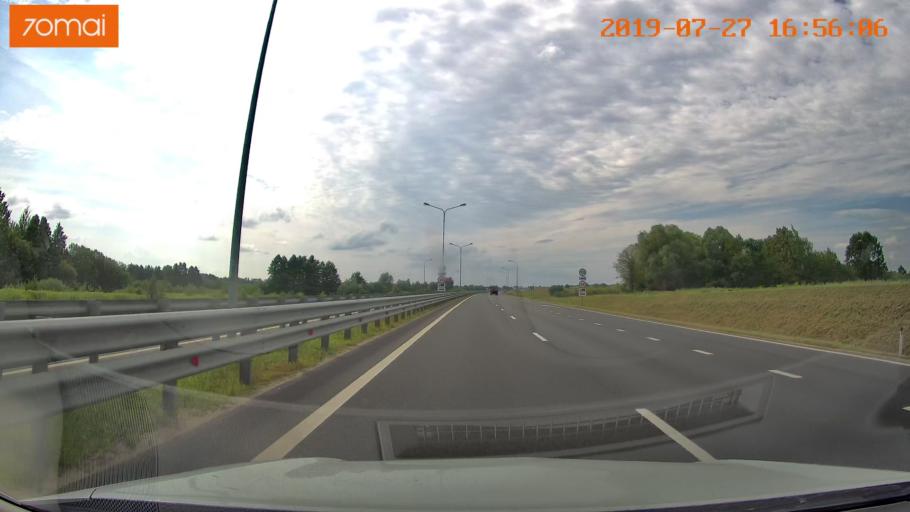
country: RU
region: Kaliningrad
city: Bol'shoe Isakovo
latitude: 54.6934
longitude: 20.7501
